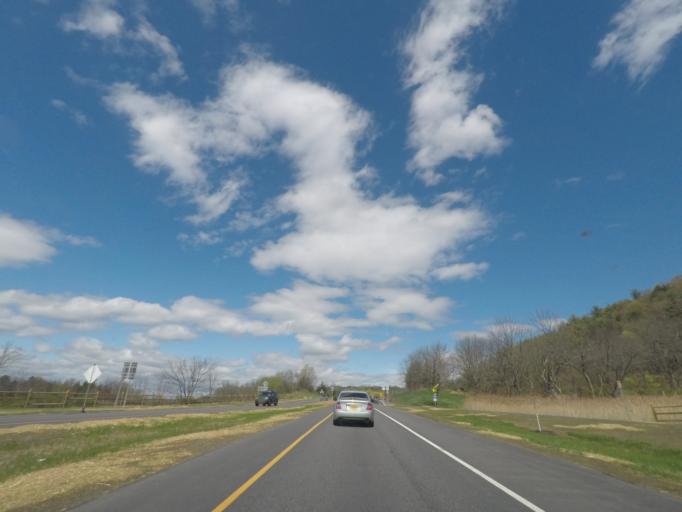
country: US
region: New York
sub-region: Greene County
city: Catskill
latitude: 42.2202
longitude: -73.8324
